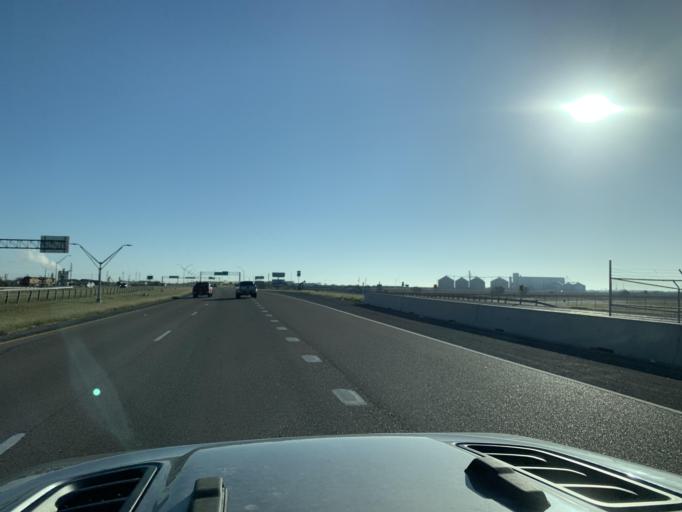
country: US
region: Texas
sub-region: Nueces County
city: Corpus Christi
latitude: 27.7848
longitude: -97.4966
